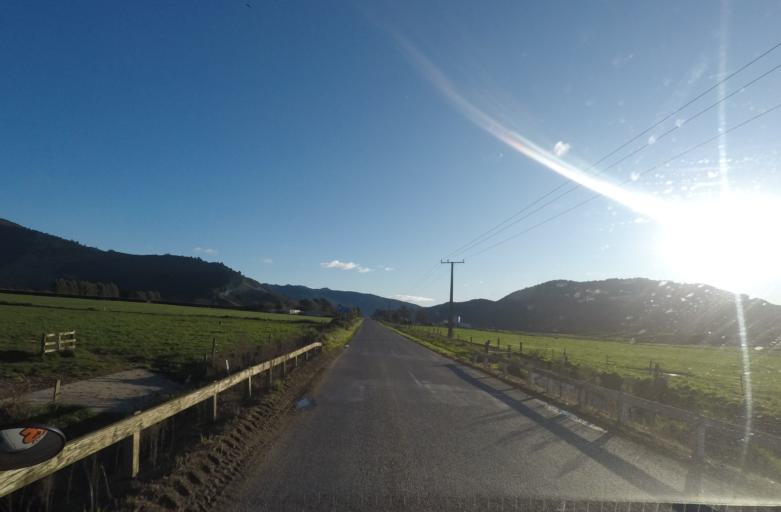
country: NZ
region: Marlborough
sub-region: Marlborough District
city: Picton
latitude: -41.2896
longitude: 173.8722
